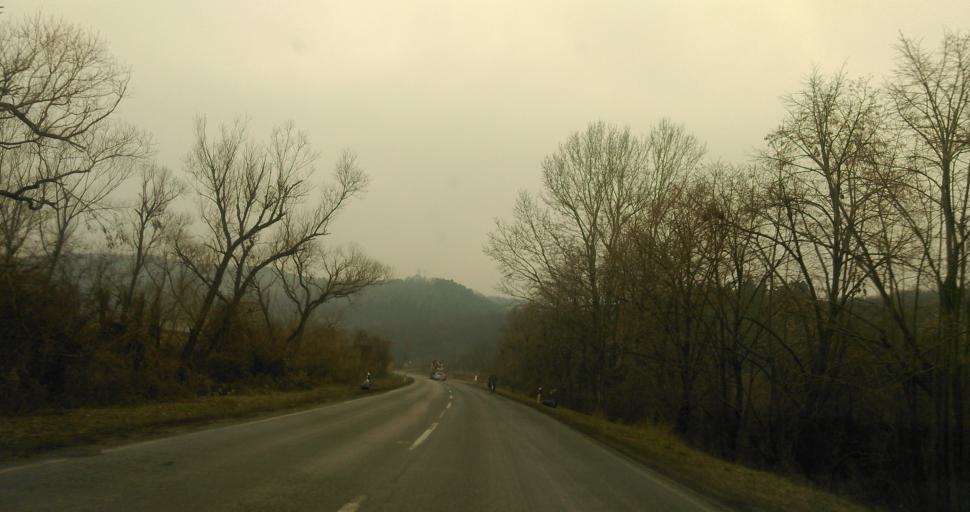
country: RS
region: Central Serbia
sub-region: Belgrade
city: Zvezdara
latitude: 44.7344
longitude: 20.5525
